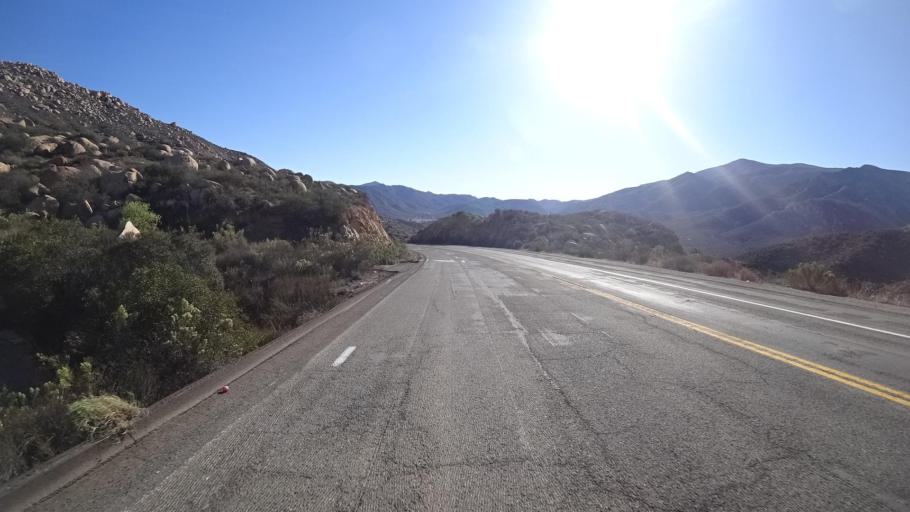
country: MX
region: Baja California
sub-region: Tecate
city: Lomas de Santa Anita
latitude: 32.6152
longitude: -116.7228
